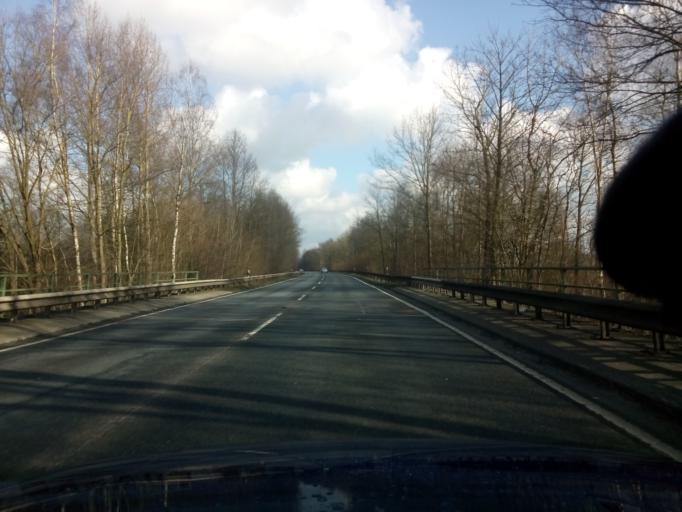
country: DE
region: Lower Saxony
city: Osterholz-Scharmbeck
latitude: 53.2413
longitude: 8.7963
